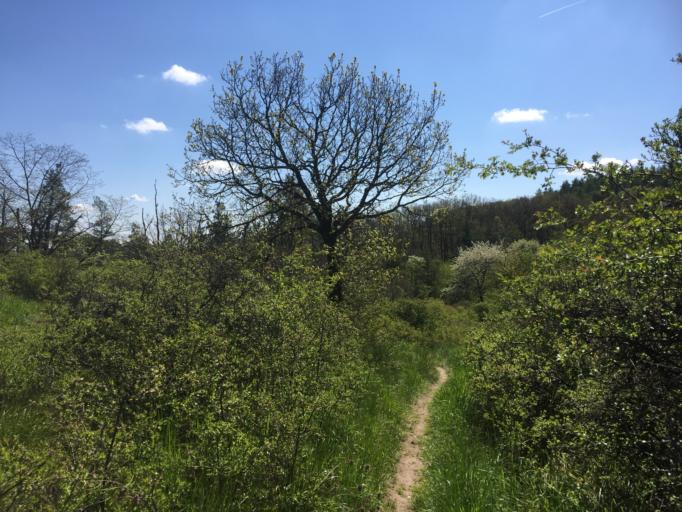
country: DE
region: Bavaria
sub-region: Regierungsbezirk Unterfranken
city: Sulzfeld
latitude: 50.2722
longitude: 10.4228
